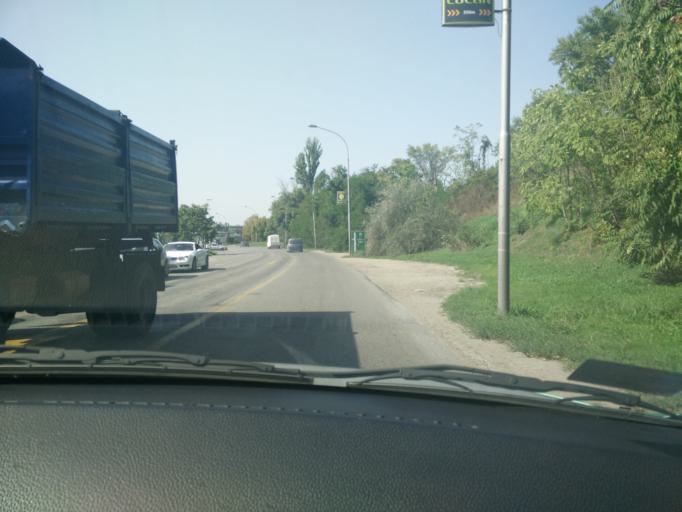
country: RS
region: Autonomna Pokrajina Vojvodina
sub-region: Juznobacki Okrug
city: Novi Sad
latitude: 45.2666
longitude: 19.8510
